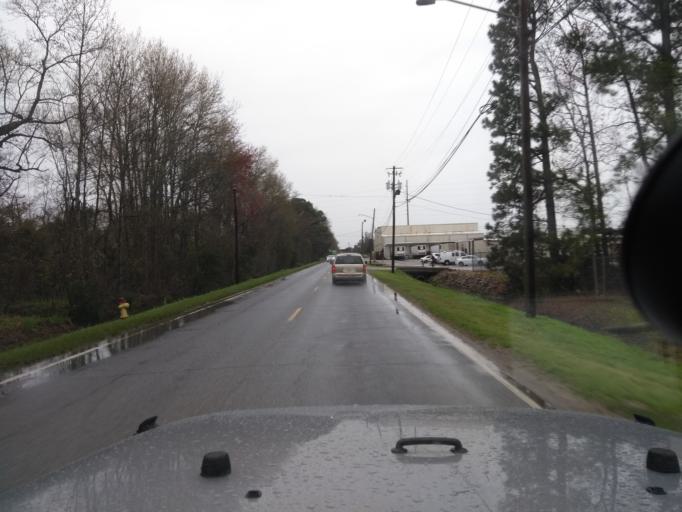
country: US
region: Georgia
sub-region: Chatham County
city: Garden City
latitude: 32.0857
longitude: -81.1371
